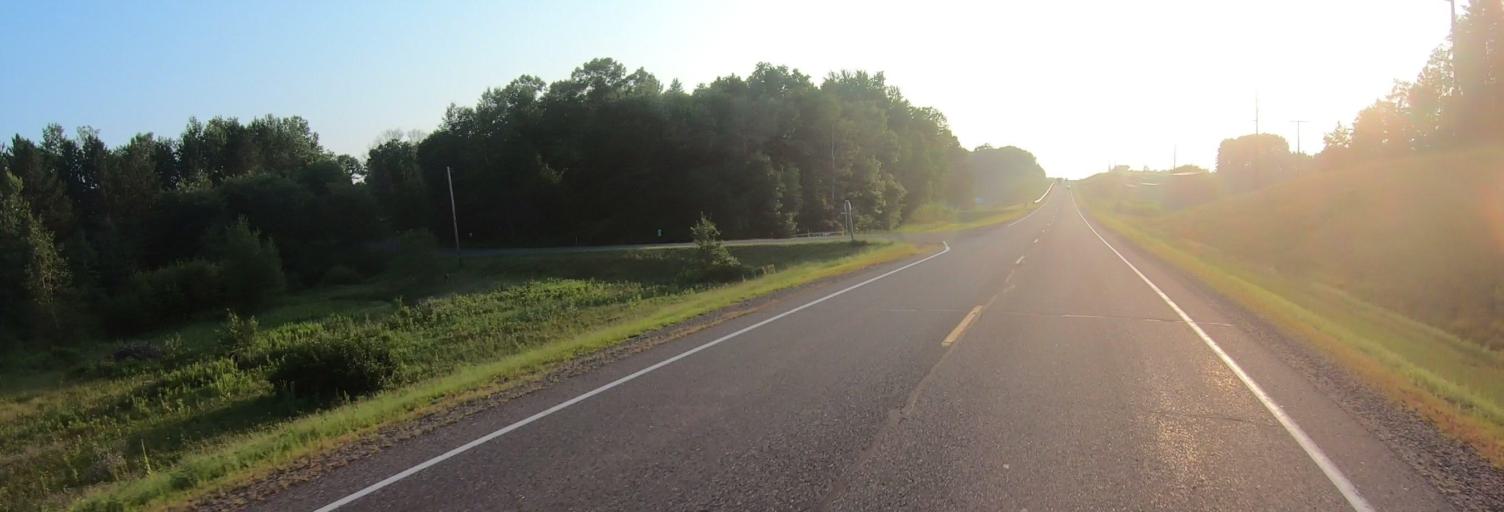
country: US
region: Wisconsin
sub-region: Washburn County
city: Shell Lake
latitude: 45.8154
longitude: -92.0634
